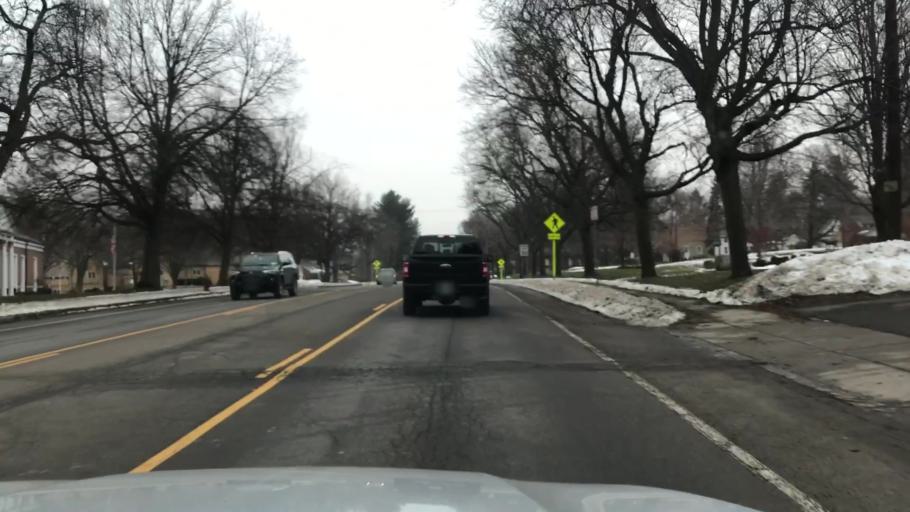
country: US
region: New York
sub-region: Erie County
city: Orchard Park
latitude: 42.7584
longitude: -78.7457
